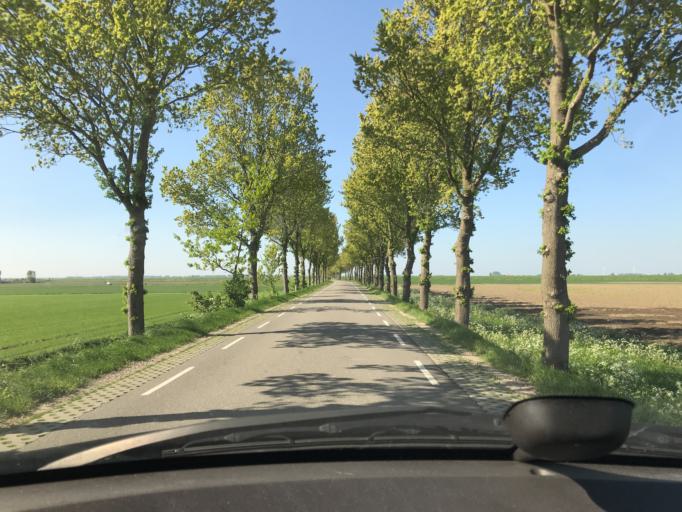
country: NL
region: Zeeland
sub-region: Gemeente Goes
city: Goes
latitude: 51.5335
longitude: 3.8531
